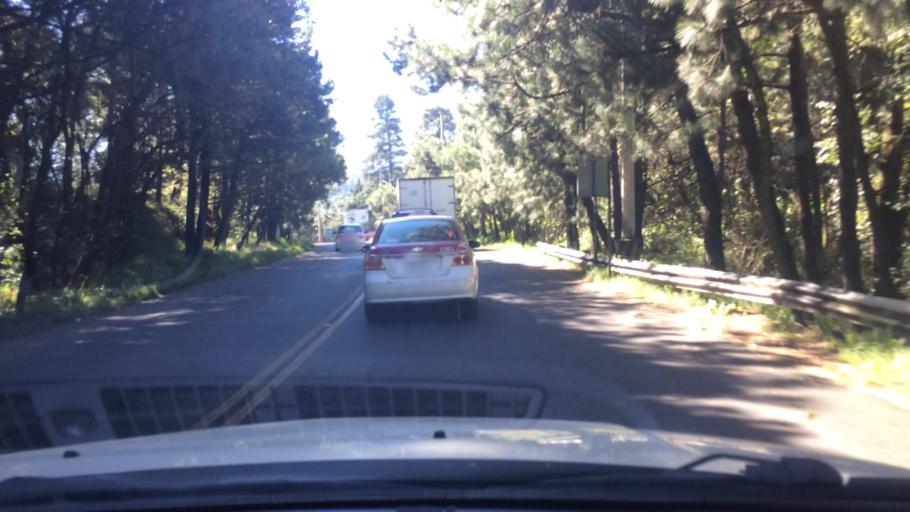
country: MX
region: Mexico City
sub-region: Tlalpan
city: Lomas de Tepemecatl
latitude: 19.2546
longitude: -99.2446
